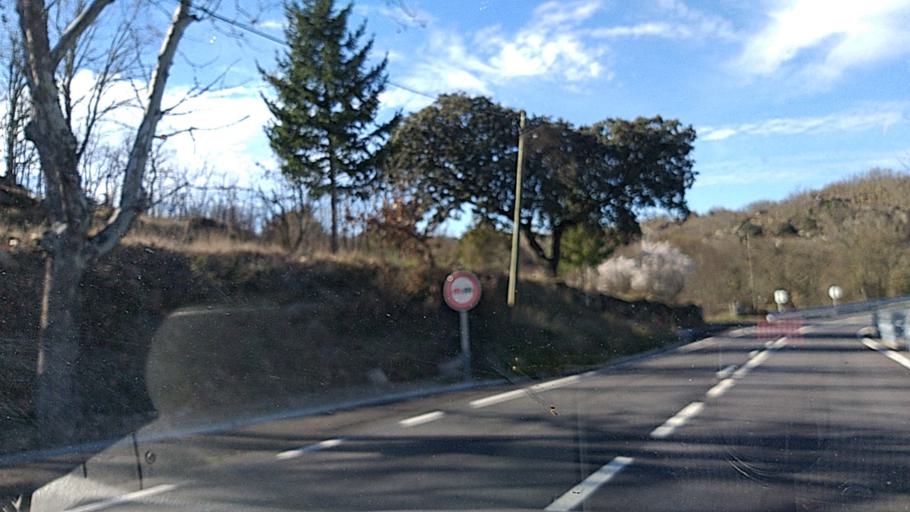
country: ES
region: Castille and Leon
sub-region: Provincia de Salamanca
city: Fuentes de Onoro
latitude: 40.6000
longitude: -6.9327
